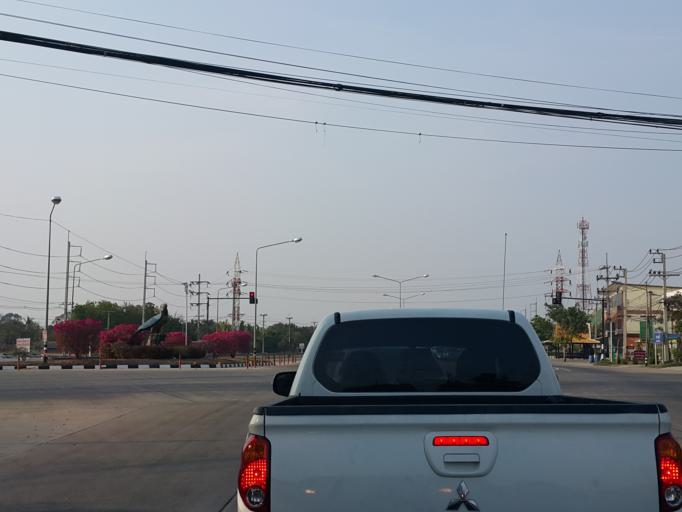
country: TH
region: Chai Nat
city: Sankhaburi
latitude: 15.0441
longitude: 100.1487
